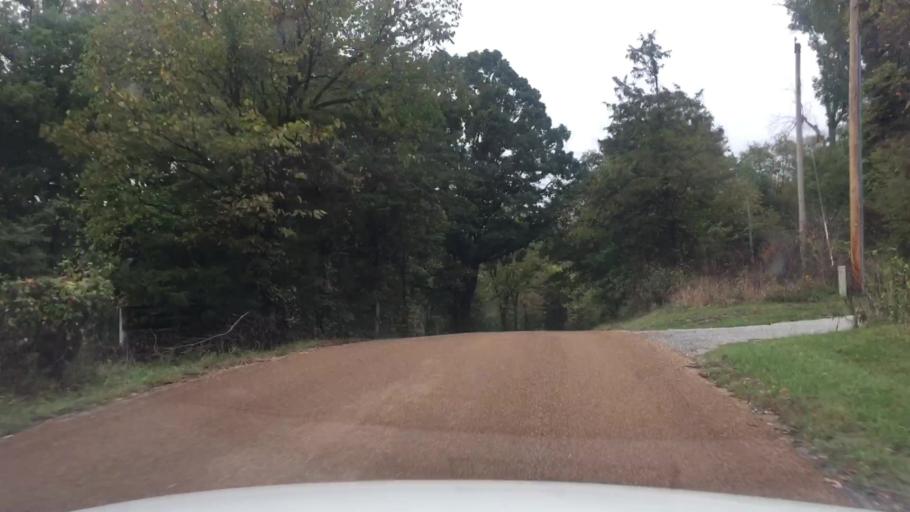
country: US
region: Missouri
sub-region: Boone County
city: Columbia
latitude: 38.8844
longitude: -92.4196
